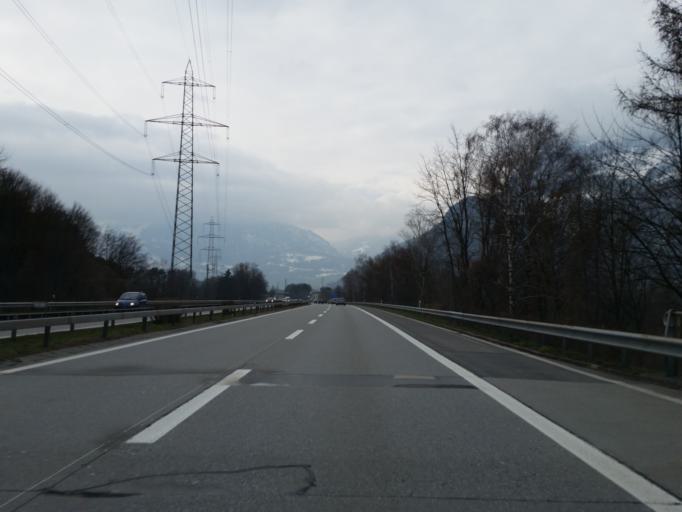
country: LI
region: Balzers
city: Balzers
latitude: 47.0795
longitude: 9.4977
